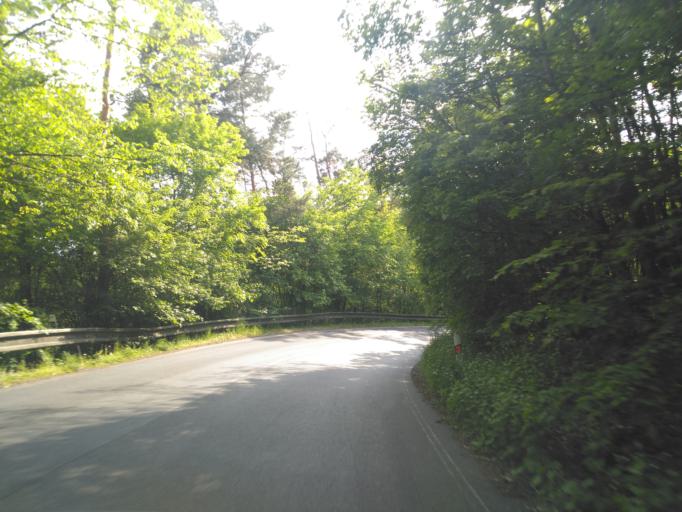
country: CZ
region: Central Bohemia
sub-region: Okres Beroun
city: Beroun
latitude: 49.9819
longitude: 14.0782
